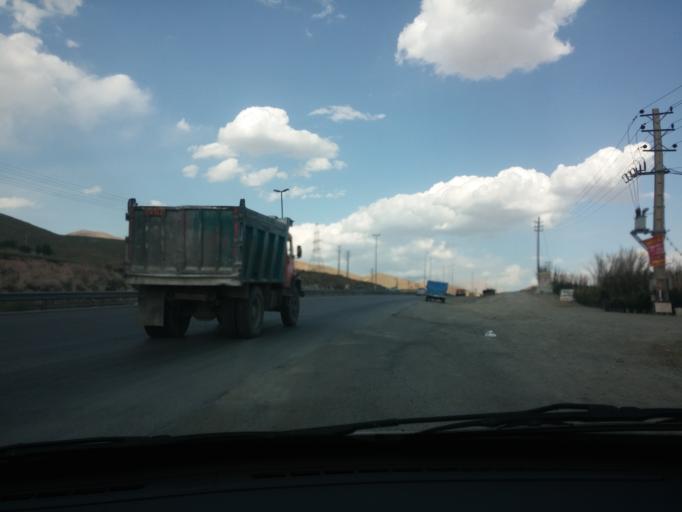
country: IR
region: Tehran
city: Damavand
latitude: 35.7076
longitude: 51.9778
